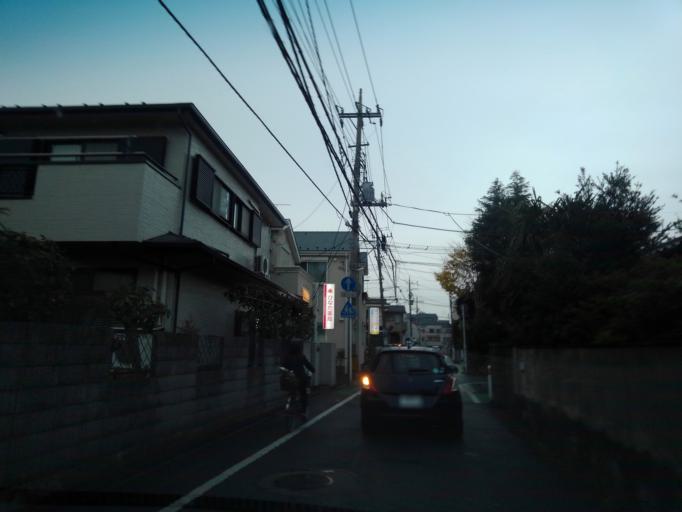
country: JP
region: Tokyo
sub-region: Machida-shi
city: Machida
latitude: 35.5163
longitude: 139.4404
